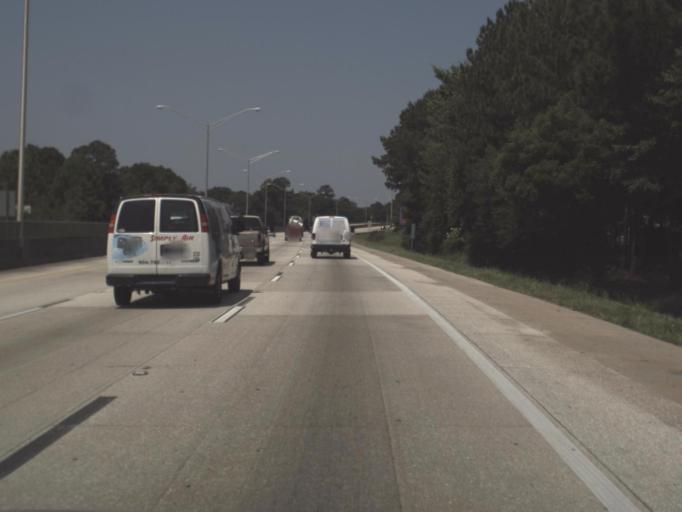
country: US
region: Florida
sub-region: Duval County
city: Jacksonville
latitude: 30.3169
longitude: -81.7375
